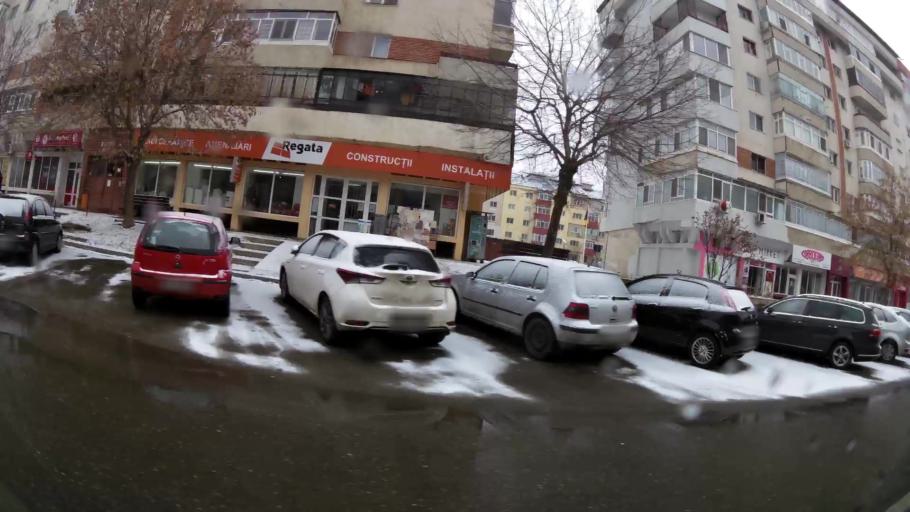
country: RO
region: Dambovita
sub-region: Municipiul Targoviste
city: Targoviste
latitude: 44.9191
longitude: 25.4787
